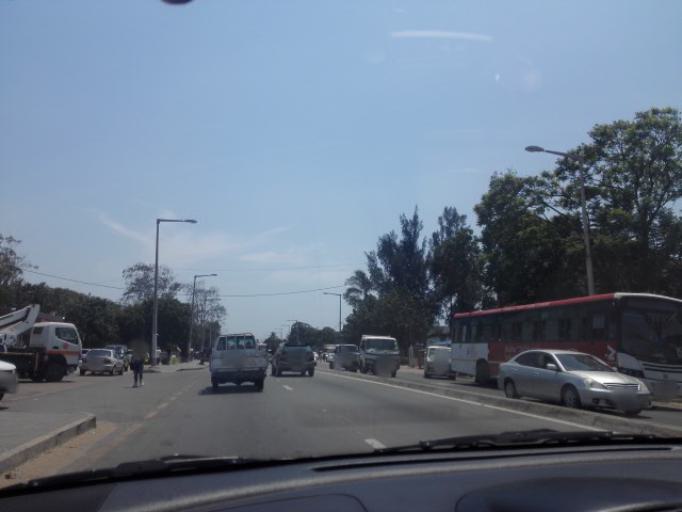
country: MZ
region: Maputo City
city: Maputo
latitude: -25.9263
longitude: 32.5580
